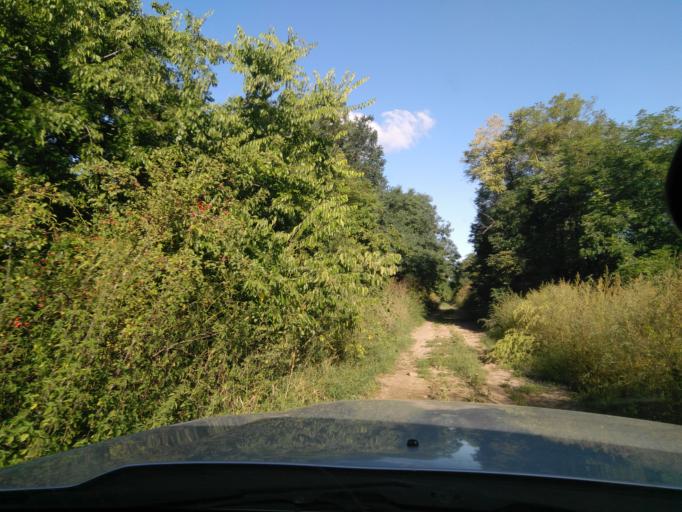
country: HU
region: Fejer
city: Kapolnasnyek
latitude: 47.2679
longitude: 18.7116
